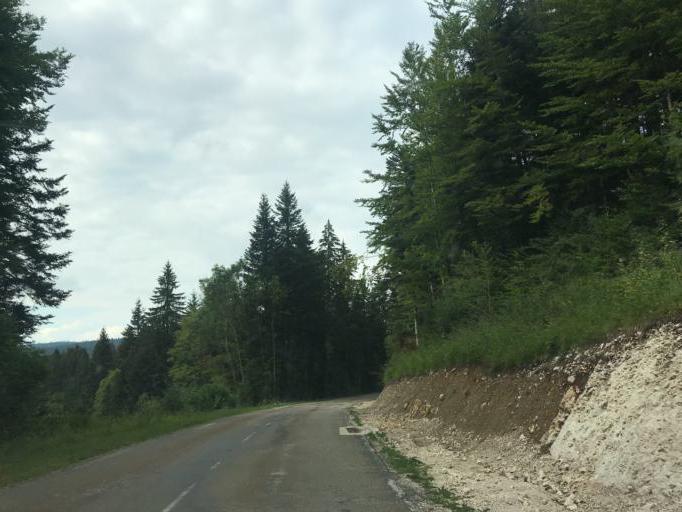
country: FR
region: Franche-Comte
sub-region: Departement du Jura
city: Longchaumois
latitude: 46.5072
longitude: 5.8860
